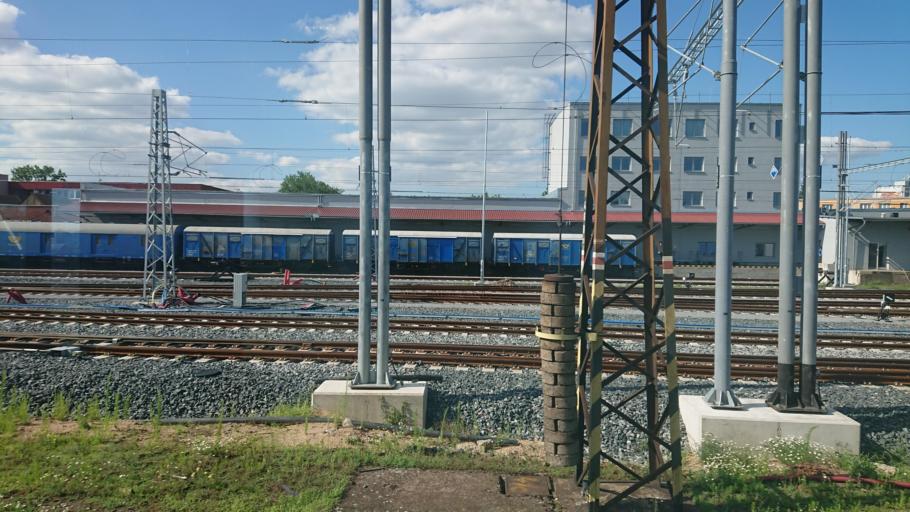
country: CZ
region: Pardubicky
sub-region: Okres Pardubice
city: Pardubice
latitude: 50.0317
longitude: 15.7608
